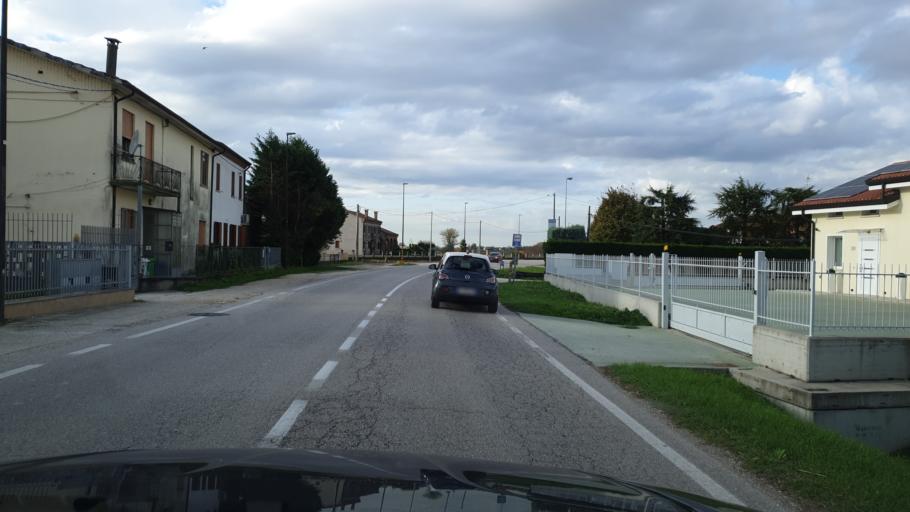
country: IT
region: Veneto
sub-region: Provincia di Rovigo
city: Villanova del Ghebbo Canton
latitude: 45.0608
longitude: 11.6315
